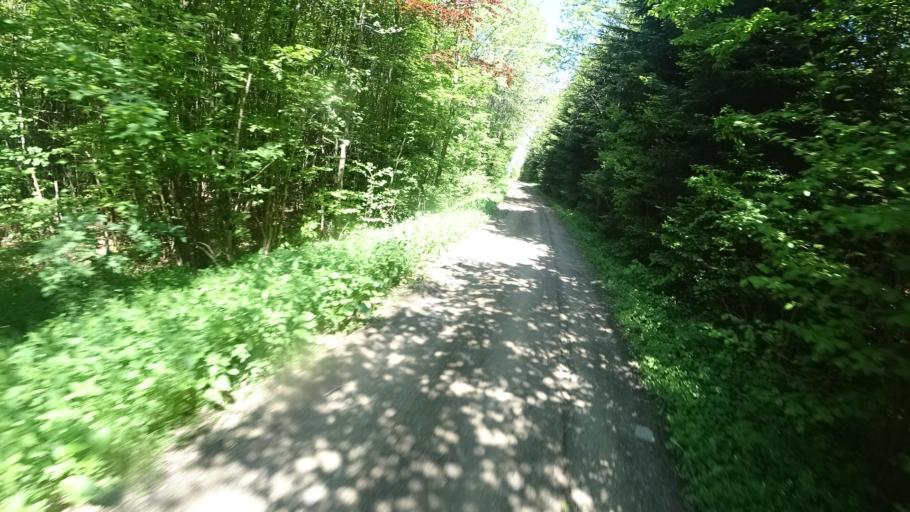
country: DE
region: Rheinland-Pfalz
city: Steineroth
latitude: 50.7544
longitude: 7.8476
